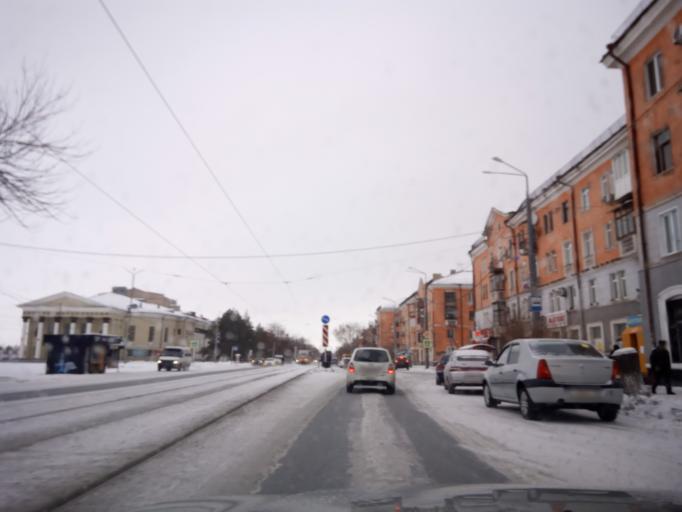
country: RU
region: Orenburg
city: Novotroitsk
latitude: 51.1957
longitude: 58.3258
